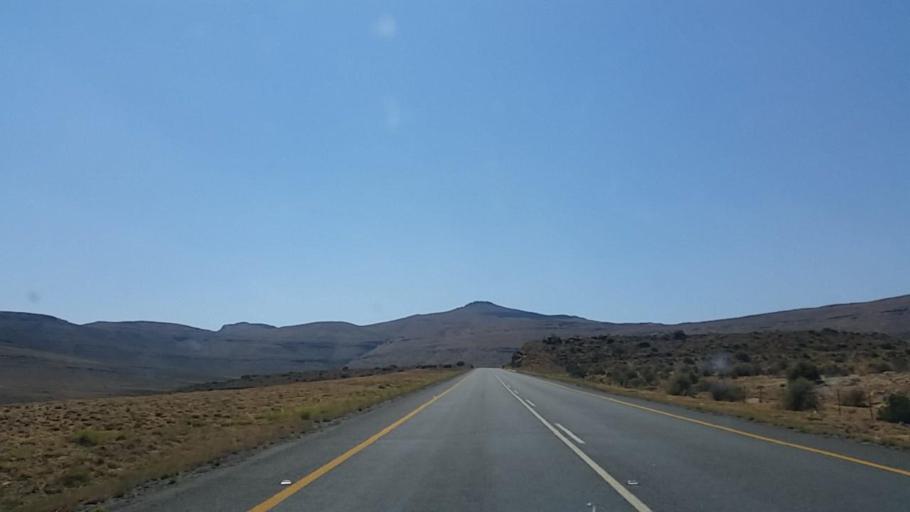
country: ZA
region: Eastern Cape
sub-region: Chris Hani District Municipality
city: Middelburg
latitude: -31.8577
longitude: 24.8635
